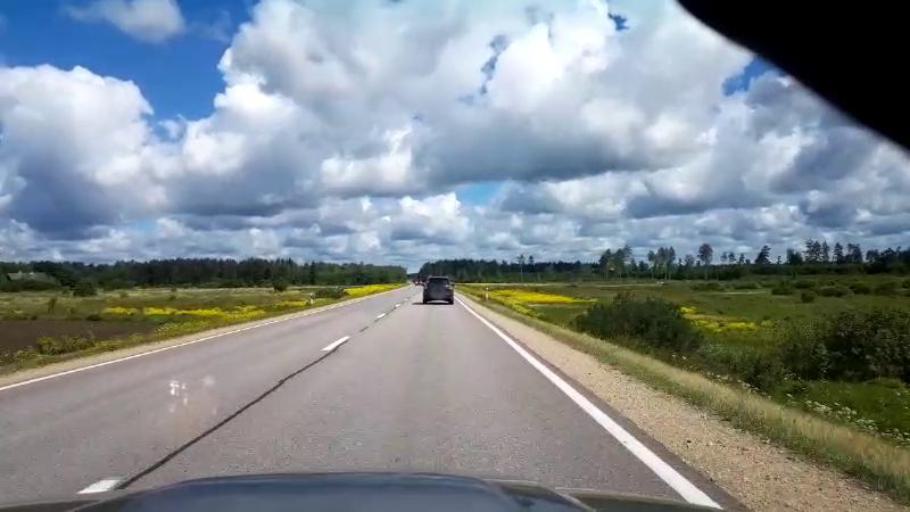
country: LV
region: Salaspils
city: Salaspils
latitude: 56.8827
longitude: 24.4077
